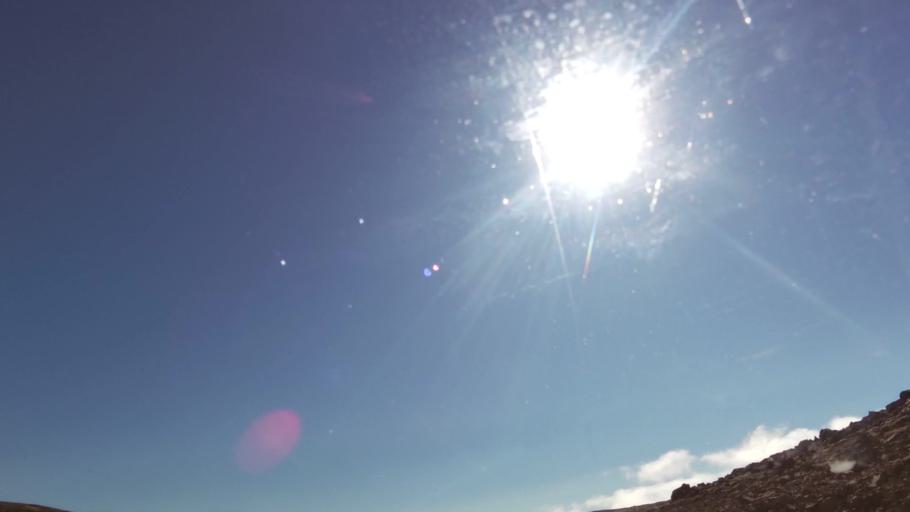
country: IS
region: West
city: Olafsvik
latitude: 65.5506
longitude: -24.2059
